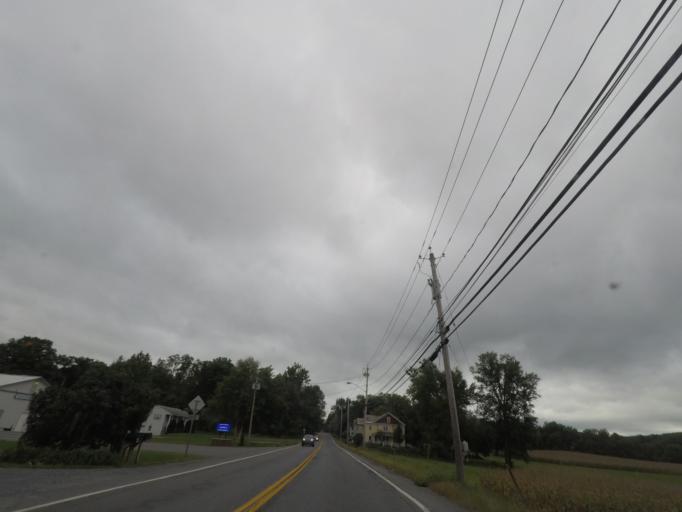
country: US
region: New York
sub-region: Rensselaer County
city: Hoosick Falls
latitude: 42.9249
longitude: -73.3475
